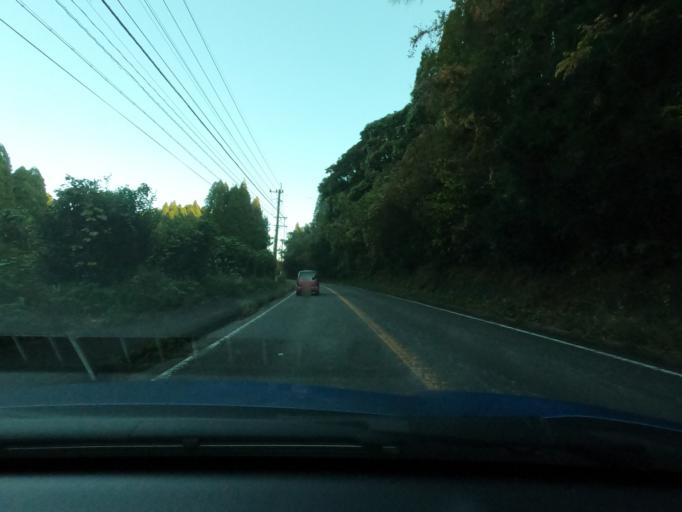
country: JP
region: Kagoshima
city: Satsumasendai
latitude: 31.8127
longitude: 130.3782
